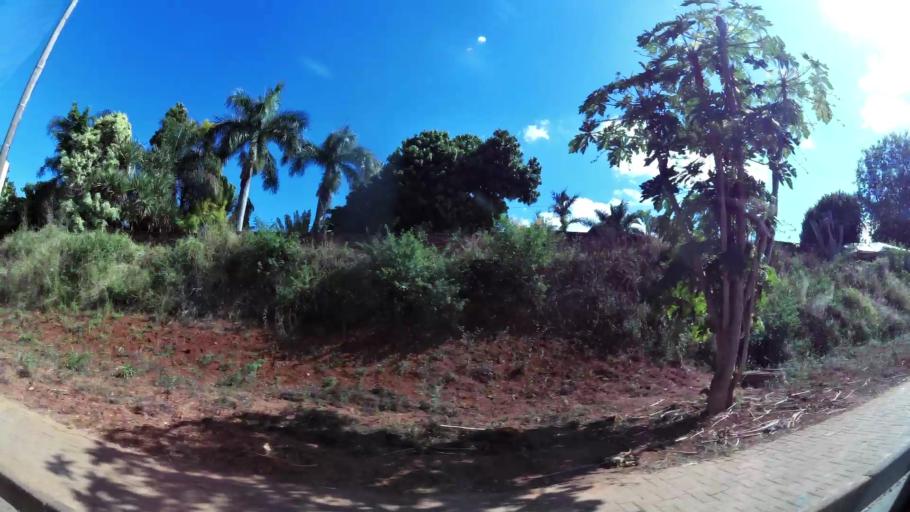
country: ZA
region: Limpopo
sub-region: Mopani District Municipality
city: Tzaneen
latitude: -23.8138
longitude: 30.1593
